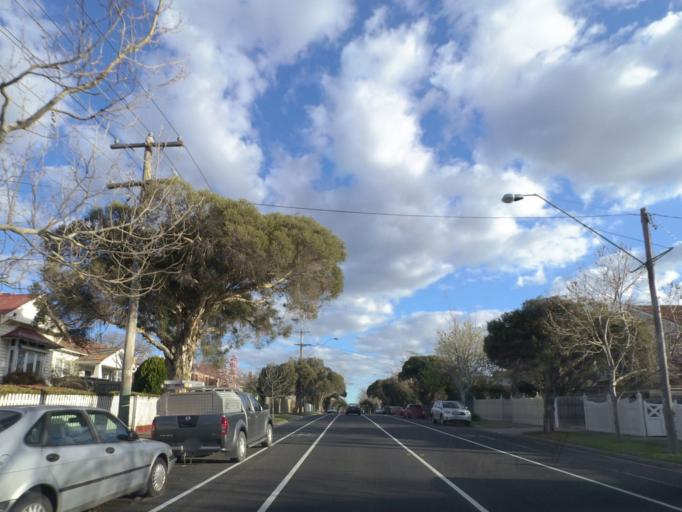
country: AU
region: Victoria
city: Mont Albert
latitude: -37.8172
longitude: 145.0990
